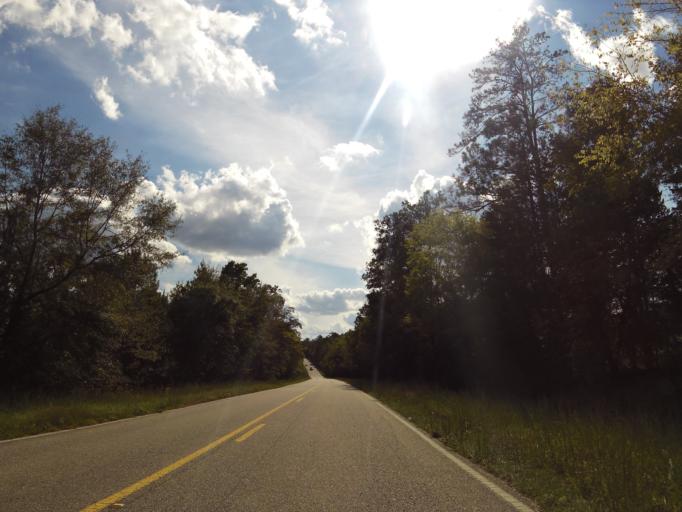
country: US
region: Alabama
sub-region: Dallas County
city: Selmont-West Selmont
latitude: 32.1802
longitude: -87.0448
